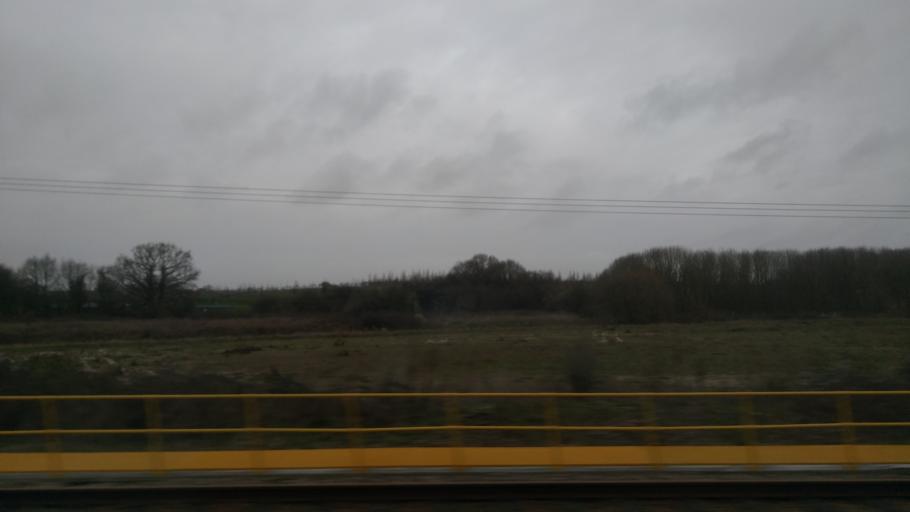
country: GB
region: England
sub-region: Kent
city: Headcorn
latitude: 51.1678
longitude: 0.6000
